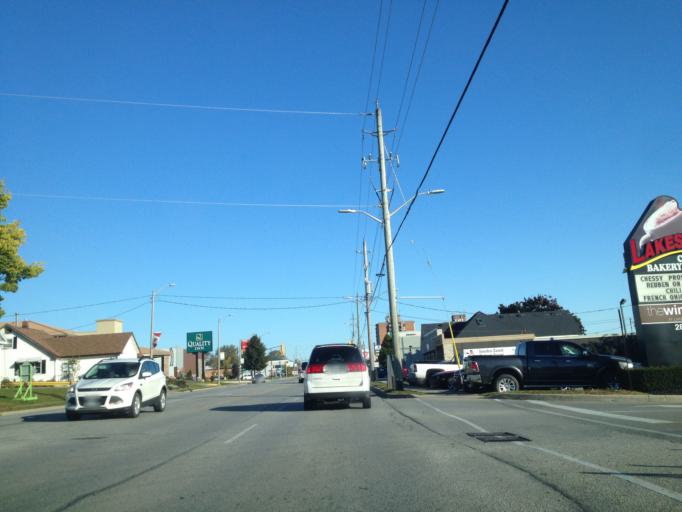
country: CA
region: Ontario
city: Amherstburg
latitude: 42.0364
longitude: -82.6008
